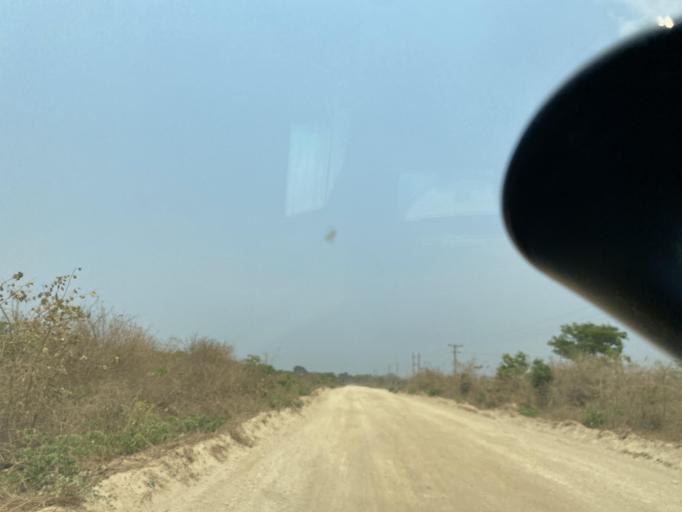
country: ZM
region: Lusaka
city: Lusaka
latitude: -15.5280
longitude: 28.3420
